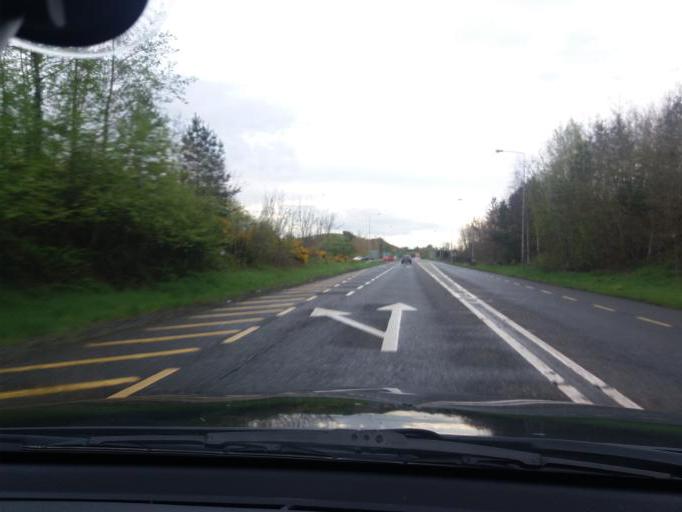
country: IE
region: Ulster
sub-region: An Cabhan
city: Cavan
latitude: 54.0453
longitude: -7.3807
